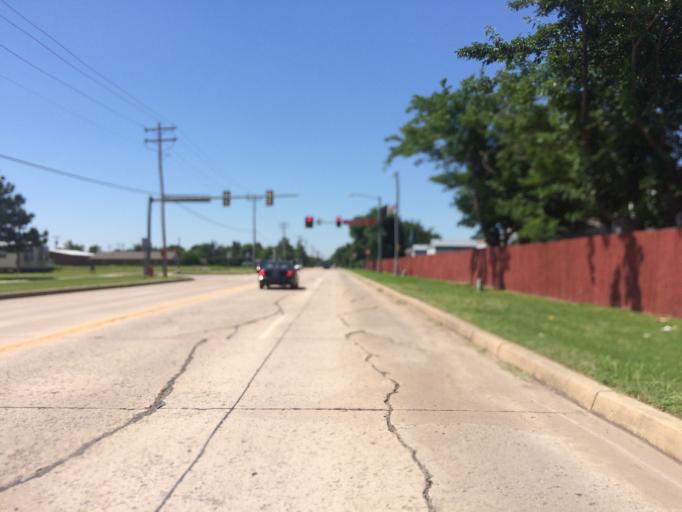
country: US
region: Oklahoma
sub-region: Cleveland County
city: Norman
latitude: 35.2392
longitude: -97.4501
